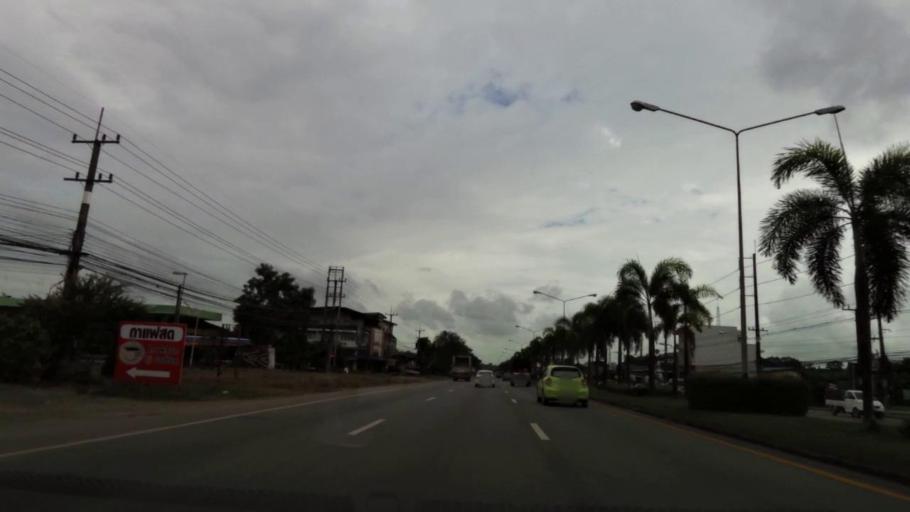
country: TH
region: Chanthaburi
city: Tha Mai
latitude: 12.7218
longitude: 101.9675
